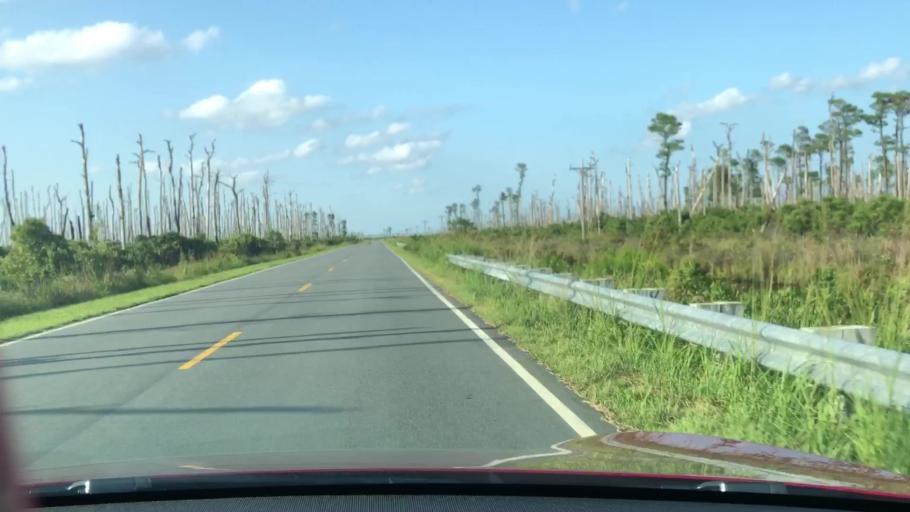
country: US
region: North Carolina
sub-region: Dare County
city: Wanchese
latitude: 35.6354
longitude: -75.7797
